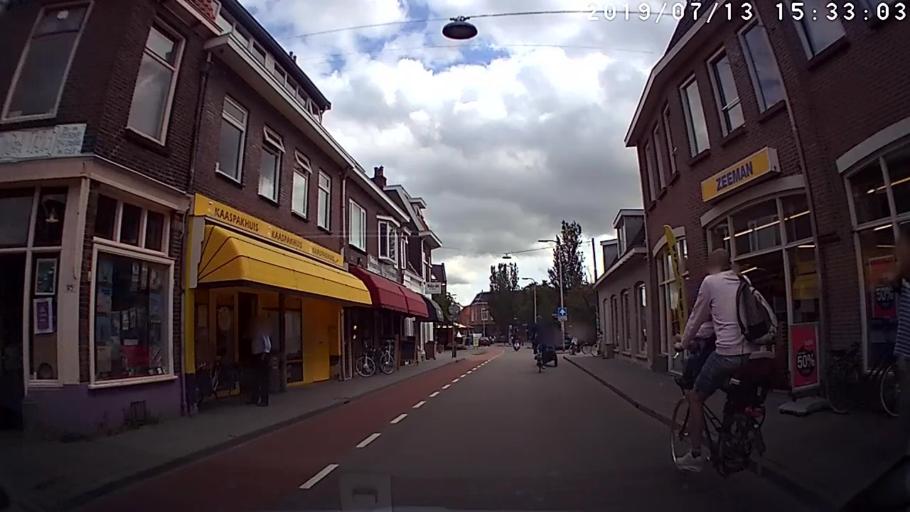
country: NL
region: Overijssel
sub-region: Gemeente Zwolle
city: Zwolle
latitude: 52.5059
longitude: 6.1021
